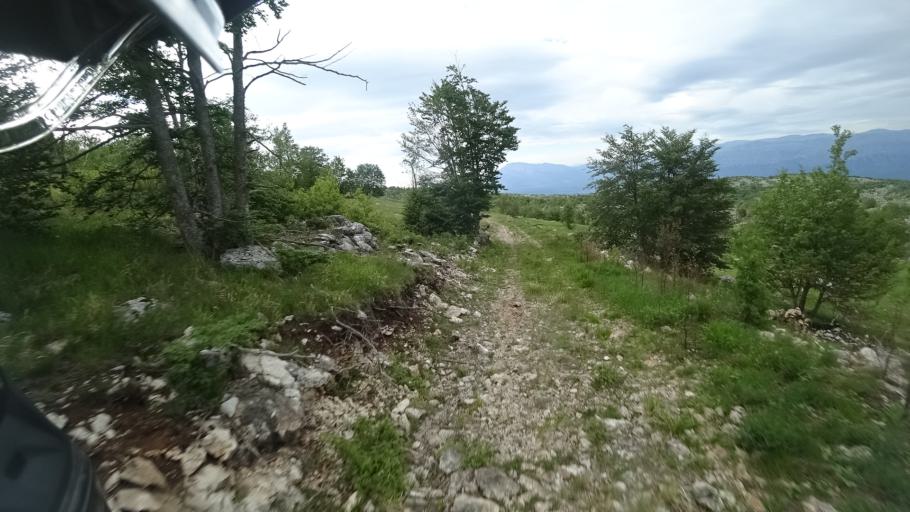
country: HR
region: Sibensko-Kniniska
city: Drnis
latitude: 43.8572
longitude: 16.3861
